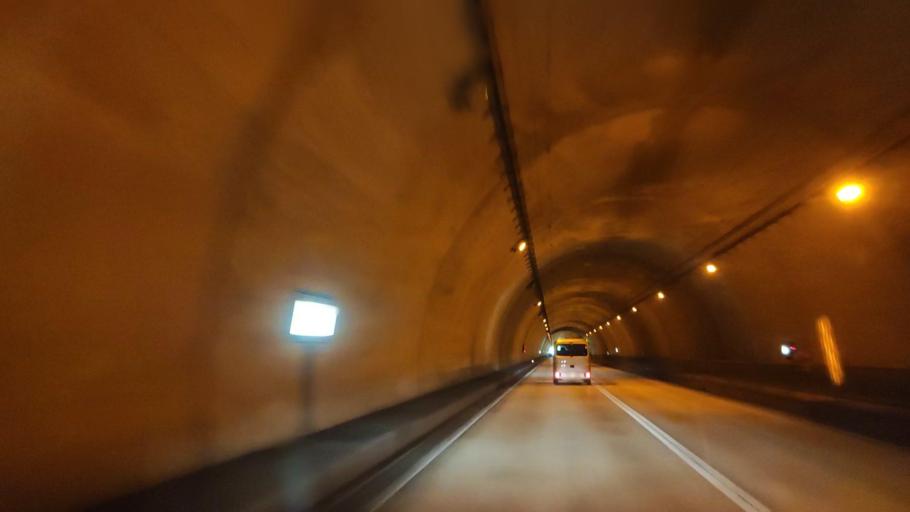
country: JP
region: Hyogo
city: Toyooka
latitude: 35.4943
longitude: 134.6238
